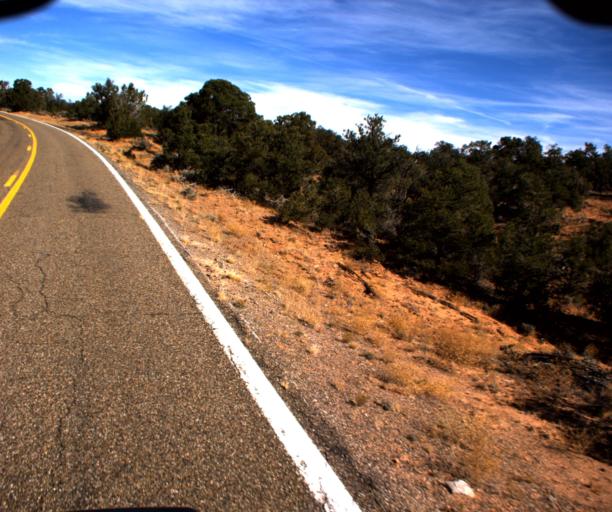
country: US
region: Arizona
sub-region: Navajo County
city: Kayenta
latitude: 36.5835
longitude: -110.4906
